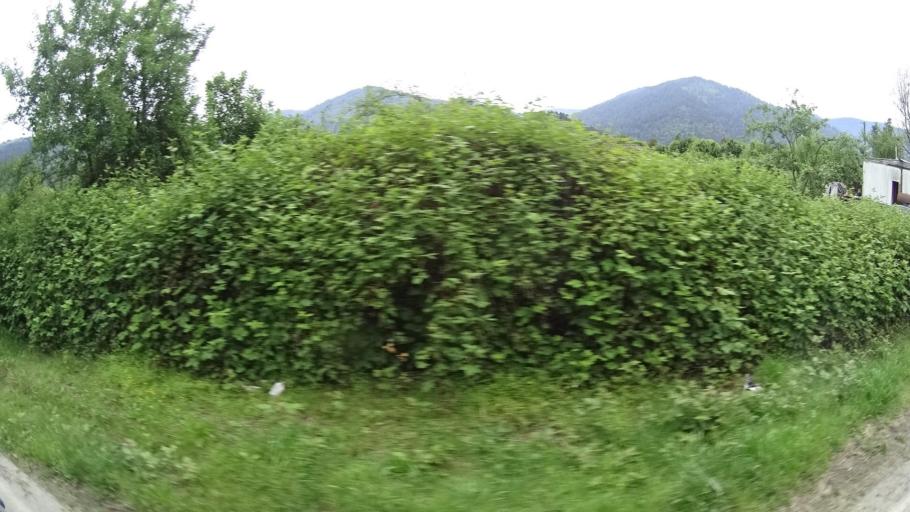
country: US
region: California
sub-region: Humboldt County
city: Willow Creek
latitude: 41.0887
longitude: -123.7121
